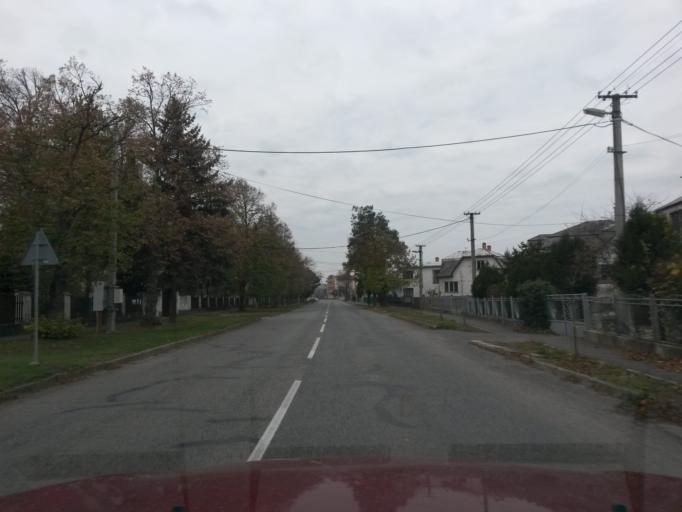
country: SK
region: Kosicky
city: Trebisov
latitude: 48.6509
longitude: 21.6780
